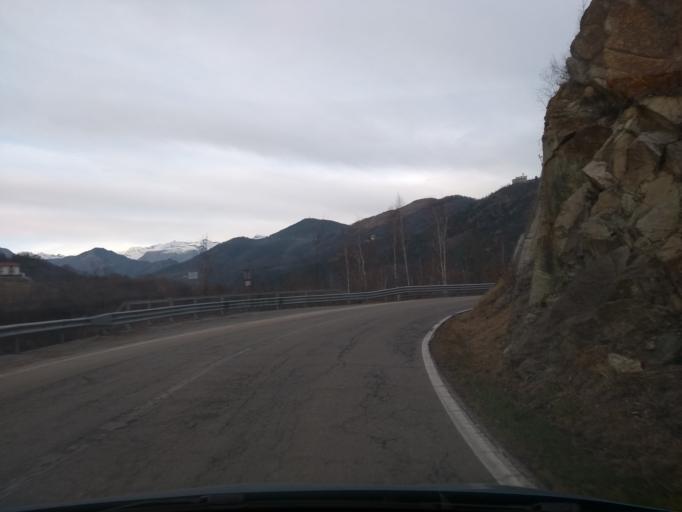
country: IT
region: Piedmont
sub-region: Provincia di Torino
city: La Villa
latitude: 45.2612
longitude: 7.4392
